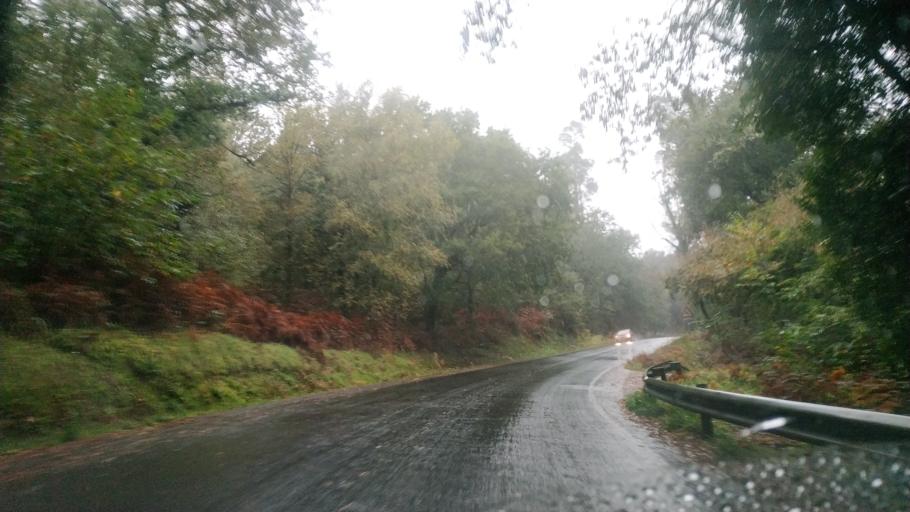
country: ES
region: Galicia
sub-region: Provincia da Coruna
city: Negreira
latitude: 42.9069
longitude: -8.7465
